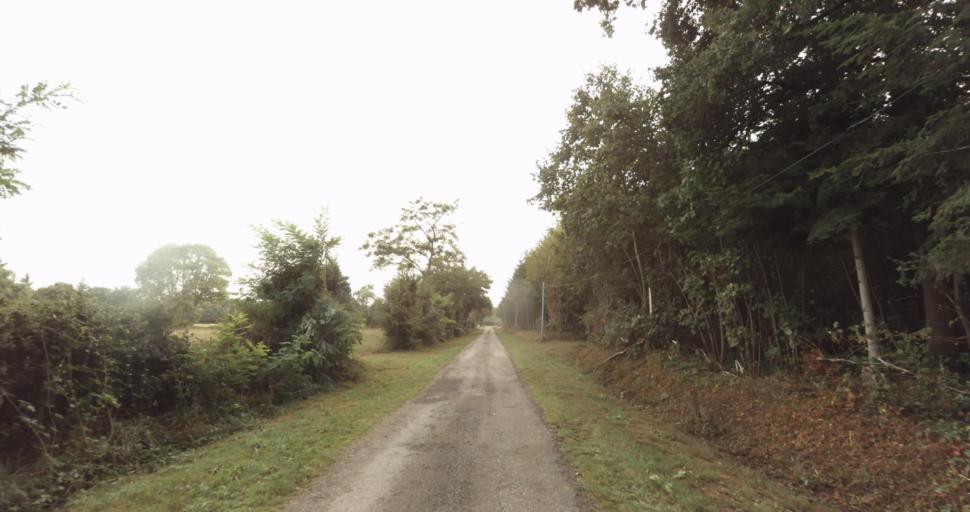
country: FR
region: Lower Normandy
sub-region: Departement de l'Orne
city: Vimoutiers
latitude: 48.9082
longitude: 0.2288
